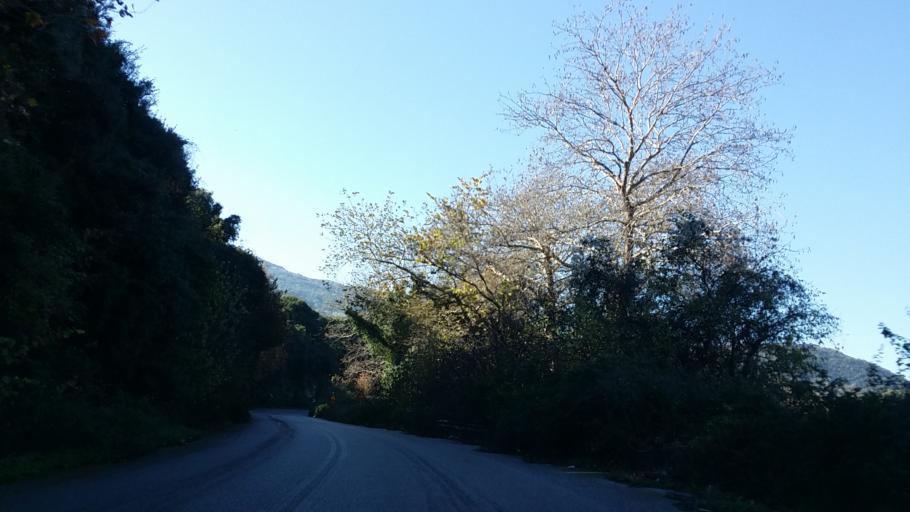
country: GR
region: West Greece
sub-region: Nomos Aitolias kai Akarnanias
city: Katouna
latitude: 38.8693
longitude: 21.0586
